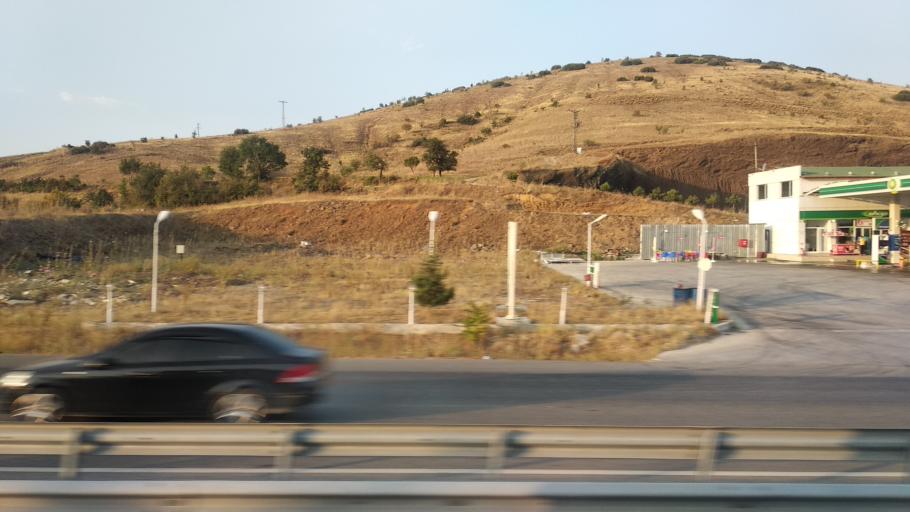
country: TR
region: Manisa
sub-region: Kula
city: Kula
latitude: 38.5666
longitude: 28.5828
